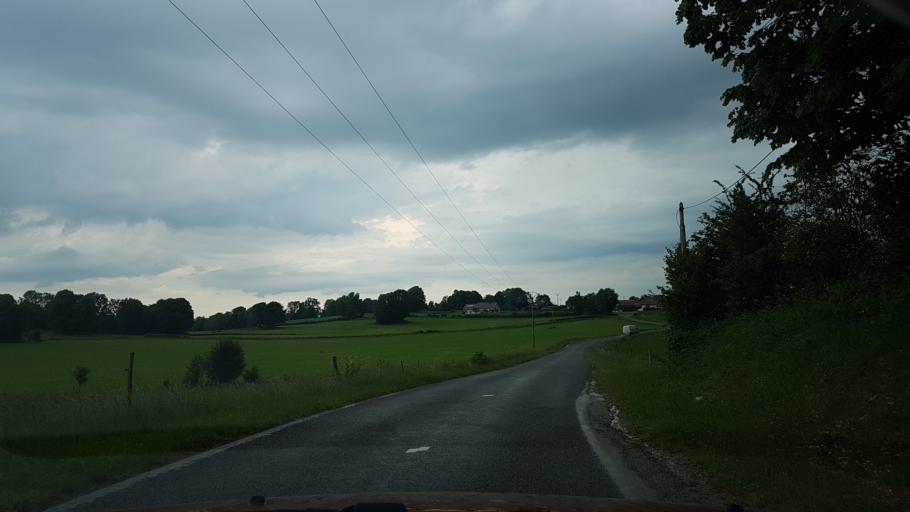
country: FR
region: Franche-Comte
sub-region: Departement du Jura
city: Clairvaux-les-Lacs
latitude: 46.5388
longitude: 5.7440
